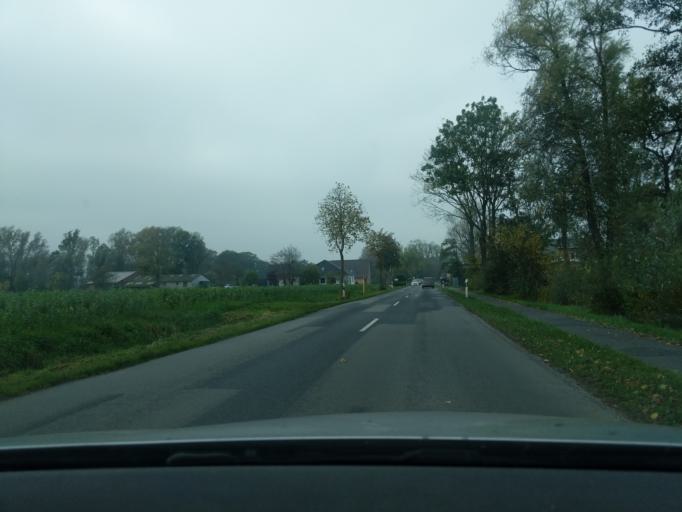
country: DE
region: Lower Saxony
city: Otterndorf
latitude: 53.8149
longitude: 8.8747
